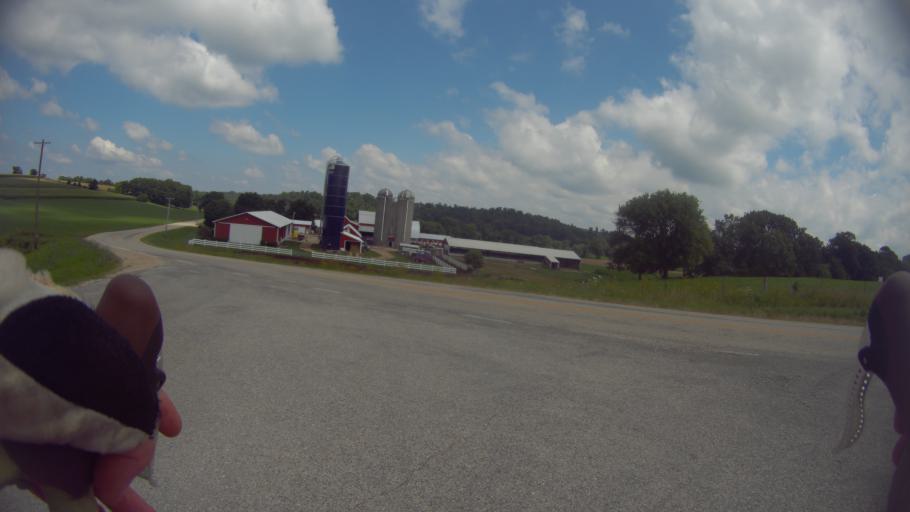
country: US
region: Wisconsin
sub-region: Columbia County
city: Lodi
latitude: 43.2427
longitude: -89.6044
